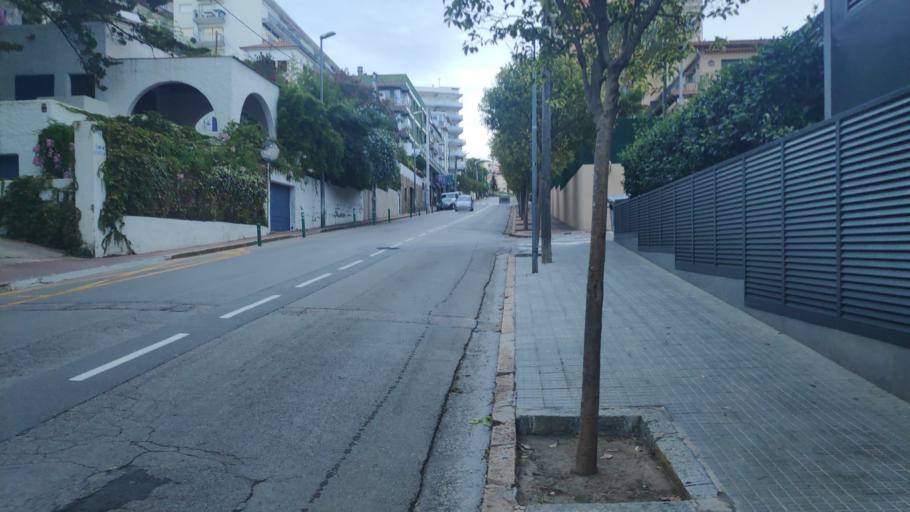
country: ES
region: Catalonia
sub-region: Provincia de Girona
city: Lloret de Mar
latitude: 41.7017
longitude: 2.8555
